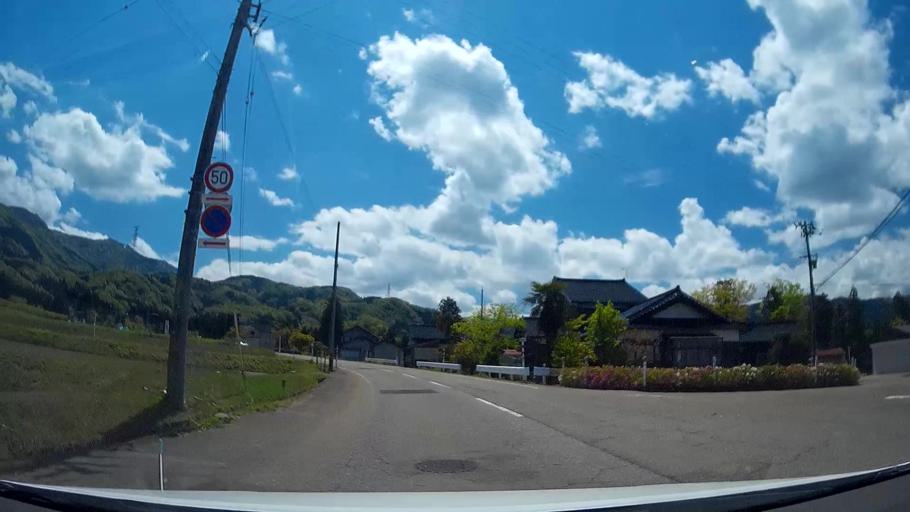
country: JP
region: Toyama
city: Fukumitsu
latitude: 36.4934
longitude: 136.8953
